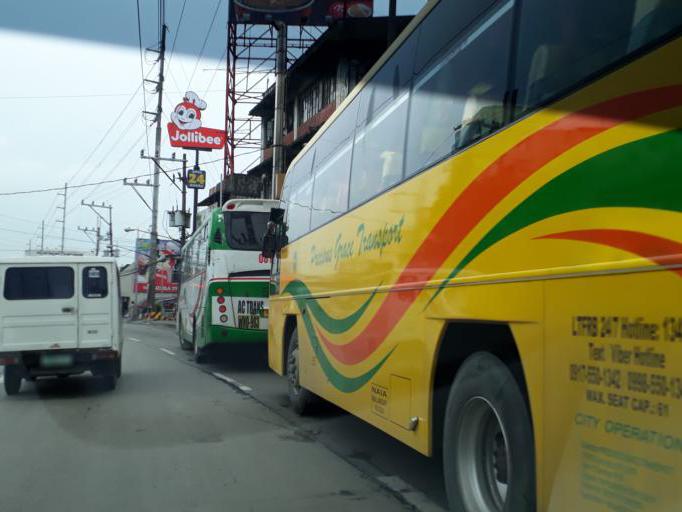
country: PH
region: Metro Manila
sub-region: Caloocan City
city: Niugan
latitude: 14.6727
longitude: 120.9821
